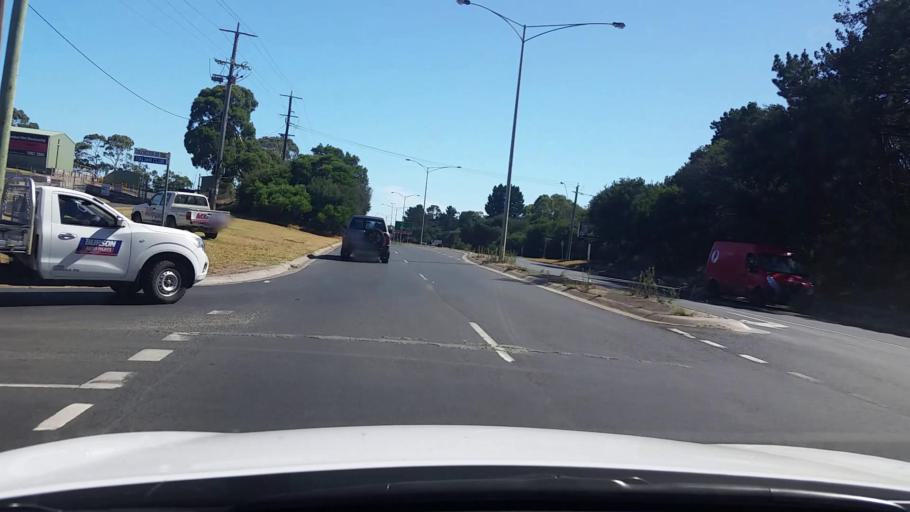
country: AU
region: Victoria
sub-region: Mornington Peninsula
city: Rosebud West
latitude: -38.3794
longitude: 144.8889
